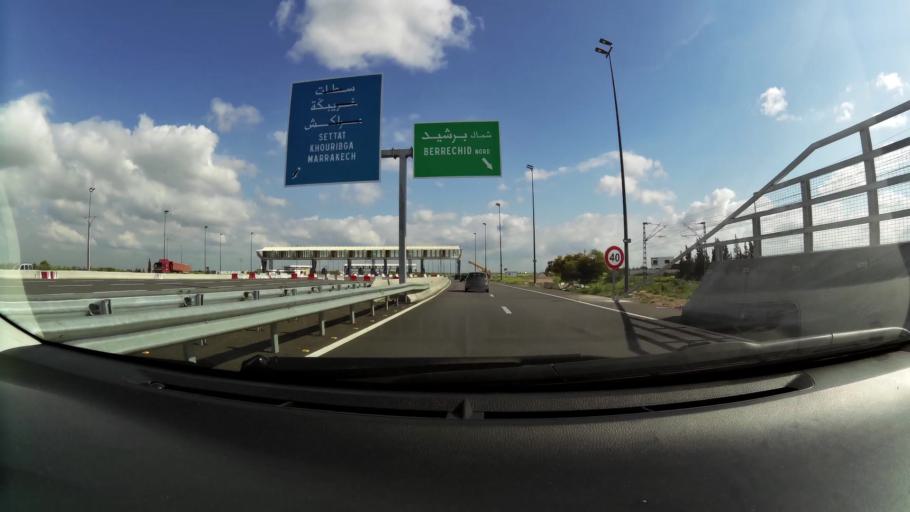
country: MA
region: Chaouia-Ouardigha
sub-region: Settat Province
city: Berrechid
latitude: 33.3216
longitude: -7.6054
